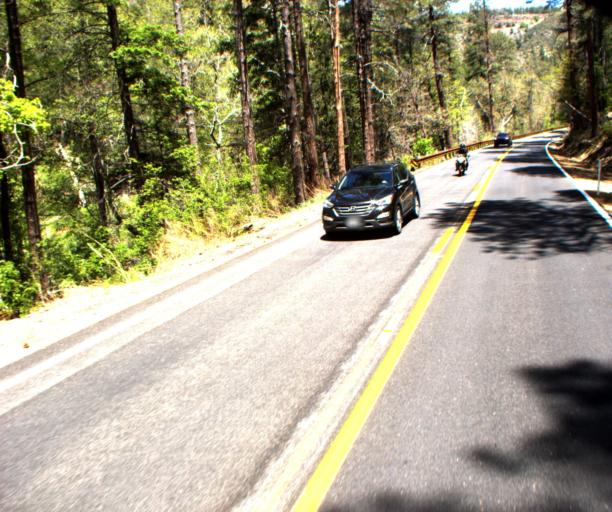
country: US
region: Arizona
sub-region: Coconino County
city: Kachina Village
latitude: 35.0180
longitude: -111.7373
